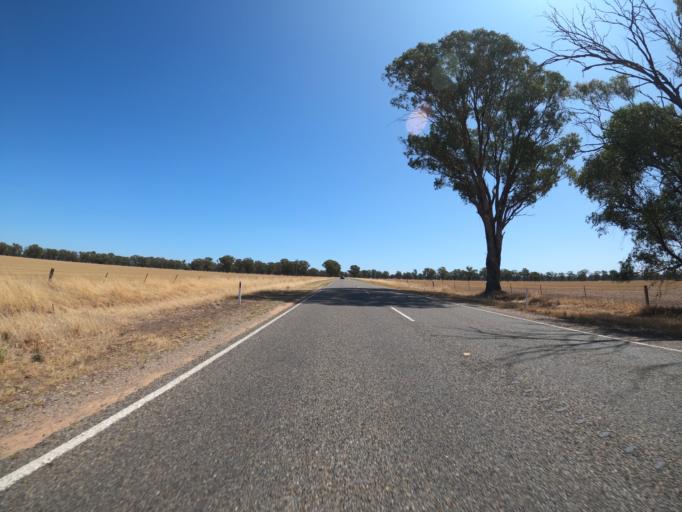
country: AU
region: New South Wales
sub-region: Corowa Shire
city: Corowa
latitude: -36.0788
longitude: 146.3419
